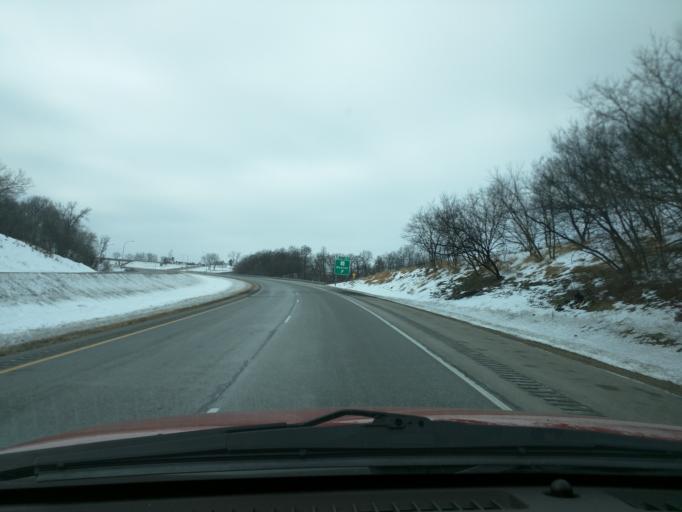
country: US
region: Wisconsin
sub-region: Trempealeau County
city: Trempealeau
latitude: 43.9301
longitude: -91.4324
